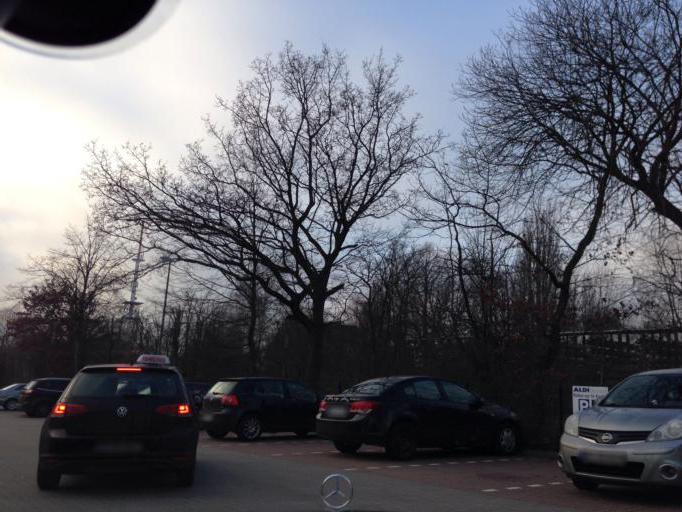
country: DE
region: Hamburg
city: Wandsbek
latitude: 53.5748
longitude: 10.1000
